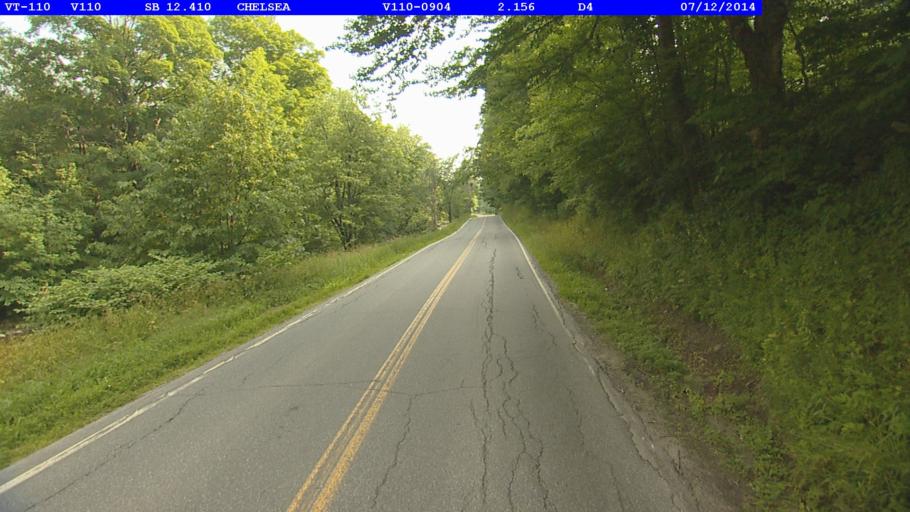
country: US
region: Vermont
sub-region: Orange County
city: Chelsea
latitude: 43.9774
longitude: -72.4482
